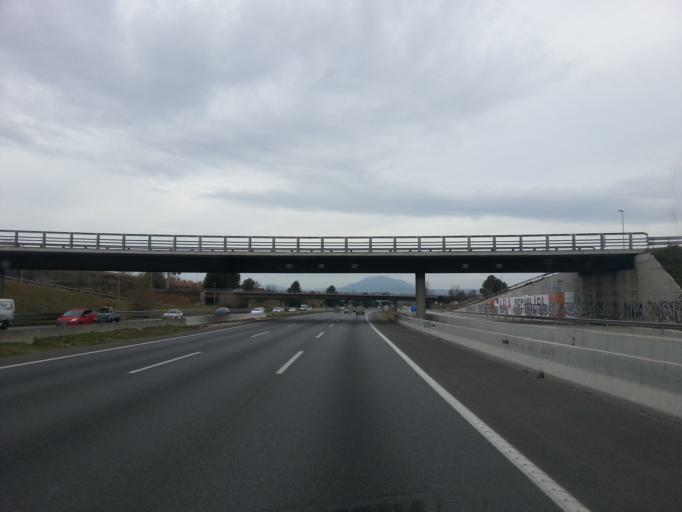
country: ES
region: Catalonia
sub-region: Provincia de Barcelona
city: Barbera del Valles
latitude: 41.5137
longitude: 2.1007
